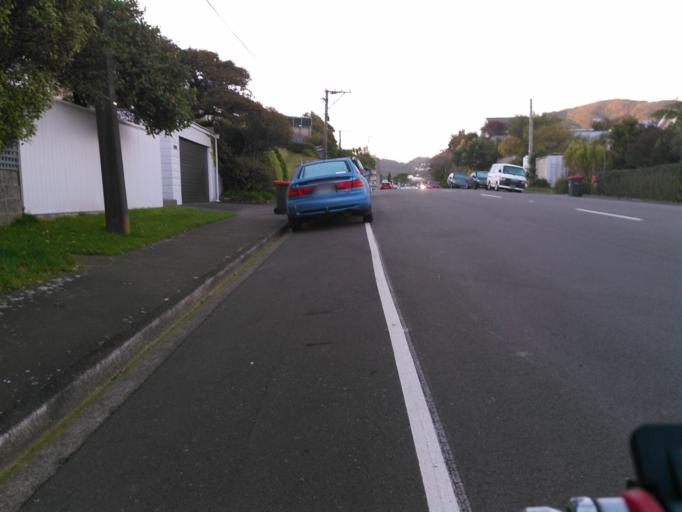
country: NZ
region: Wellington
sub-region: Wellington City
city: Kelburn
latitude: -41.2829
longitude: 174.7399
